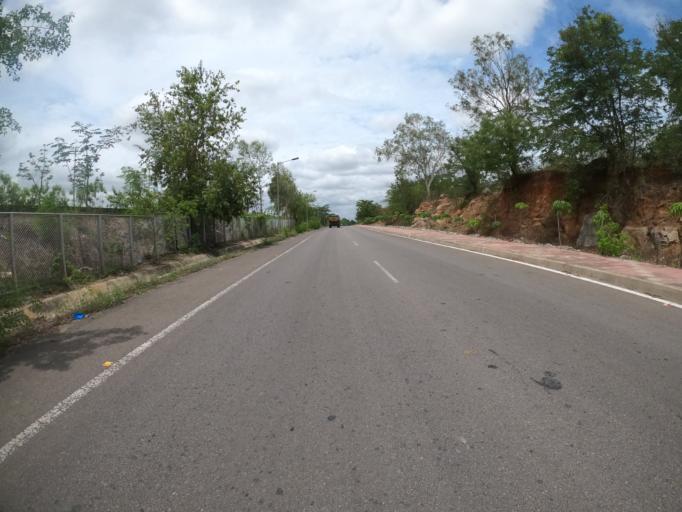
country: IN
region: Telangana
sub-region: Rangareddi
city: Balapur
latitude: 17.2767
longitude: 78.3817
